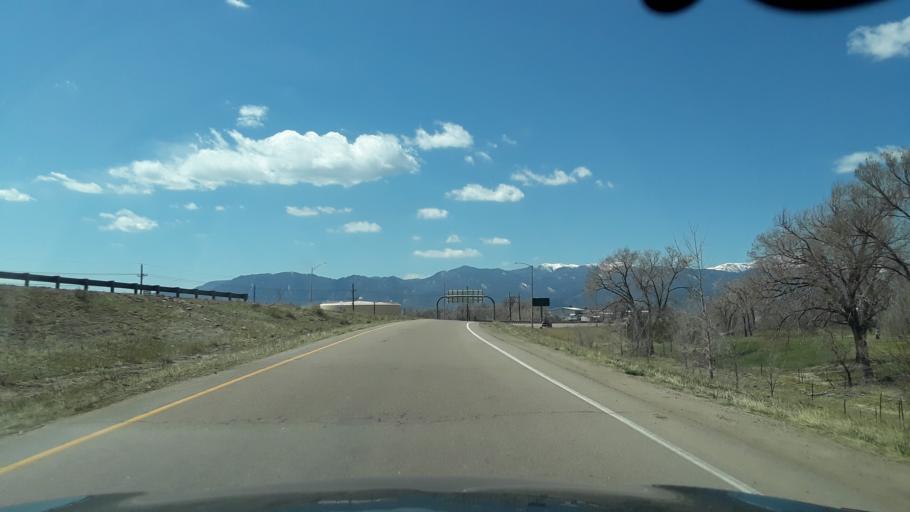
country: US
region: Colorado
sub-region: El Paso County
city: Cimarron Hills
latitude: 38.8397
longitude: -104.7029
